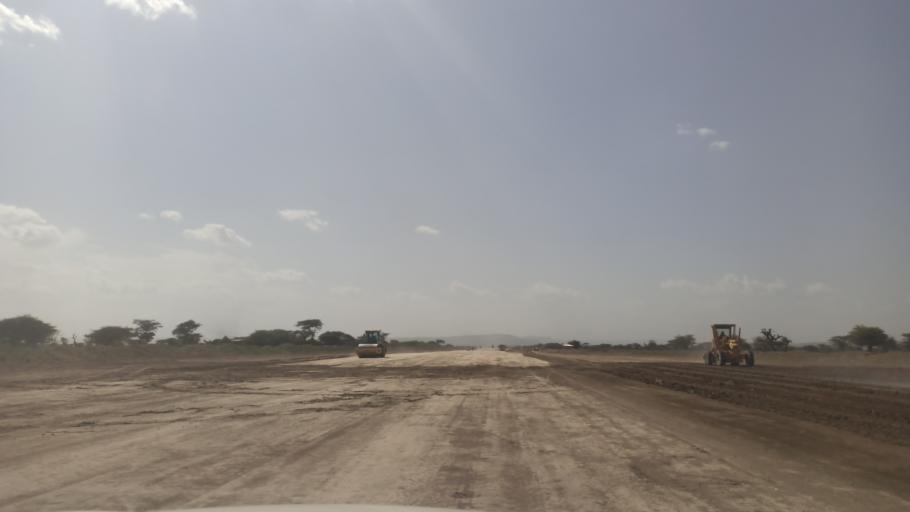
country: ET
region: Oromiya
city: Ziway
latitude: 7.7150
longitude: 38.6338
